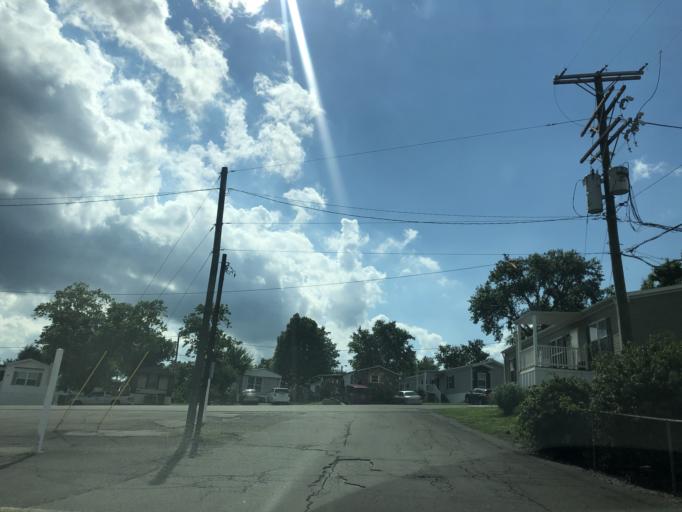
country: US
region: Tennessee
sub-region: Davidson County
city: Nashville
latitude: 36.2099
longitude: -86.7702
